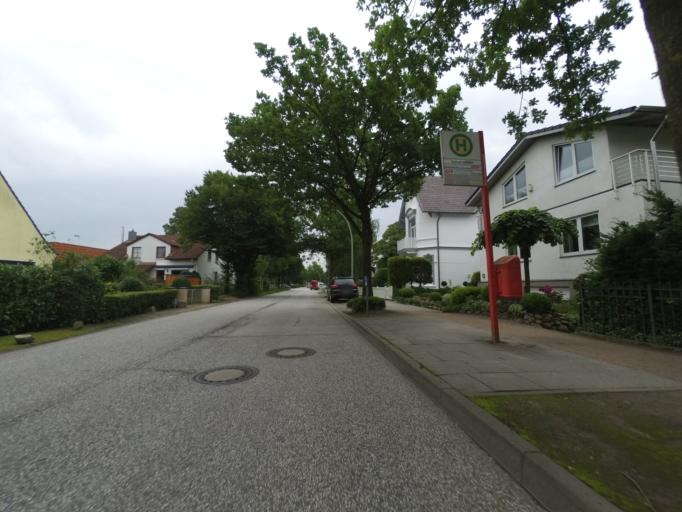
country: DE
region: Schleswig-Holstein
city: Oststeinbek
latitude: 53.5141
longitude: 10.1621
